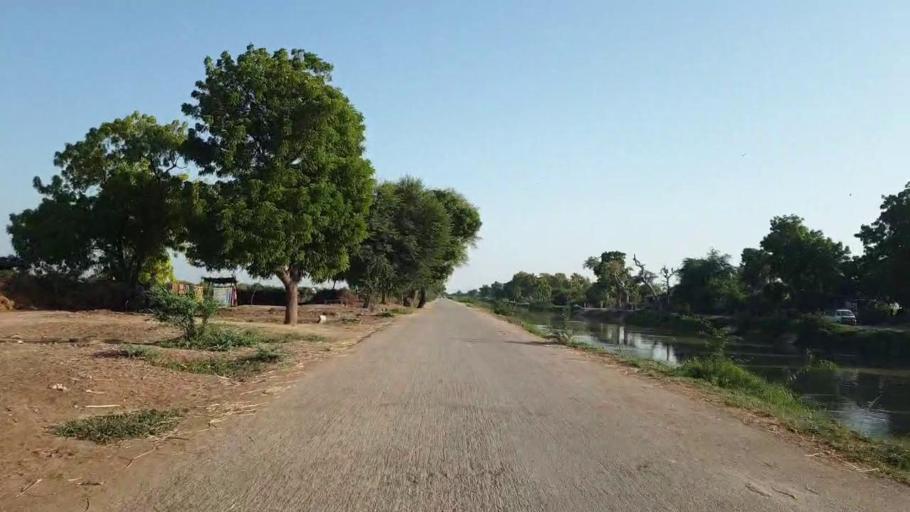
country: PK
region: Sindh
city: Hyderabad
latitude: 25.3122
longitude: 68.4315
